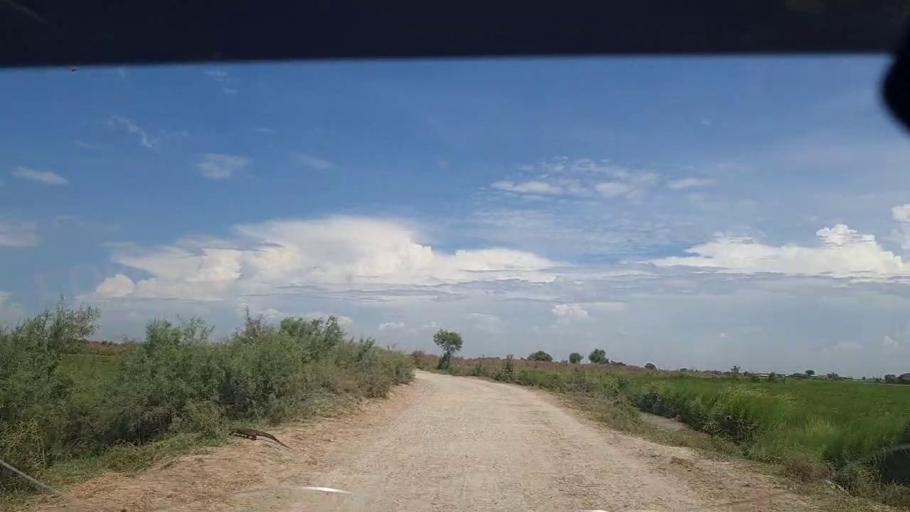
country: PK
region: Sindh
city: Ghauspur
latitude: 28.1486
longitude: 68.9697
